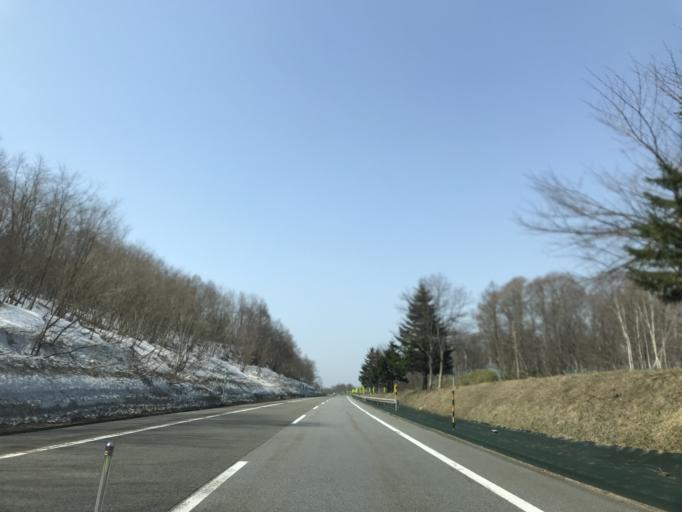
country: JP
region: Hokkaido
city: Bibai
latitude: 43.2983
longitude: 141.8740
